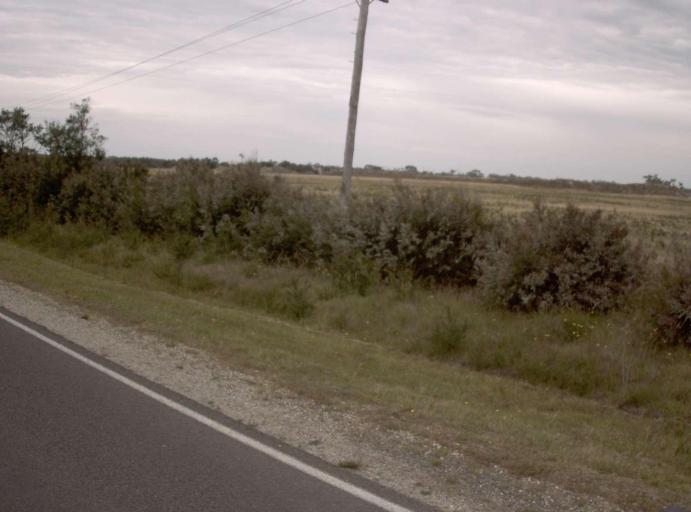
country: AU
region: Victoria
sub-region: Wellington
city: Sale
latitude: -38.1842
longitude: 147.2678
